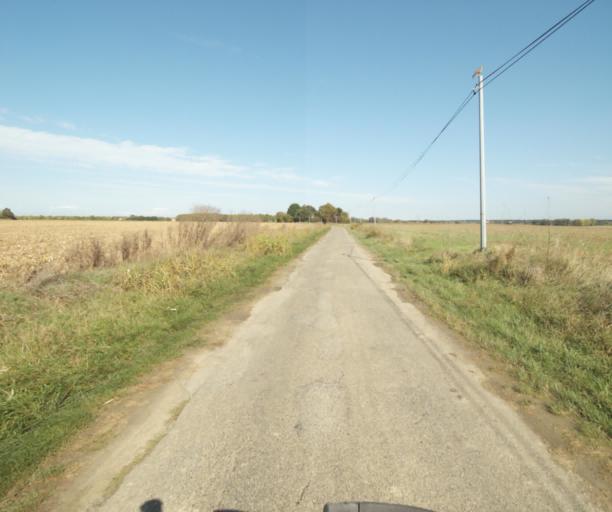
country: FR
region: Midi-Pyrenees
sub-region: Departement du Tarn-et-Garonne
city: Verdun-sur-Garonne
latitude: 43.8731
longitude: 1.2349
